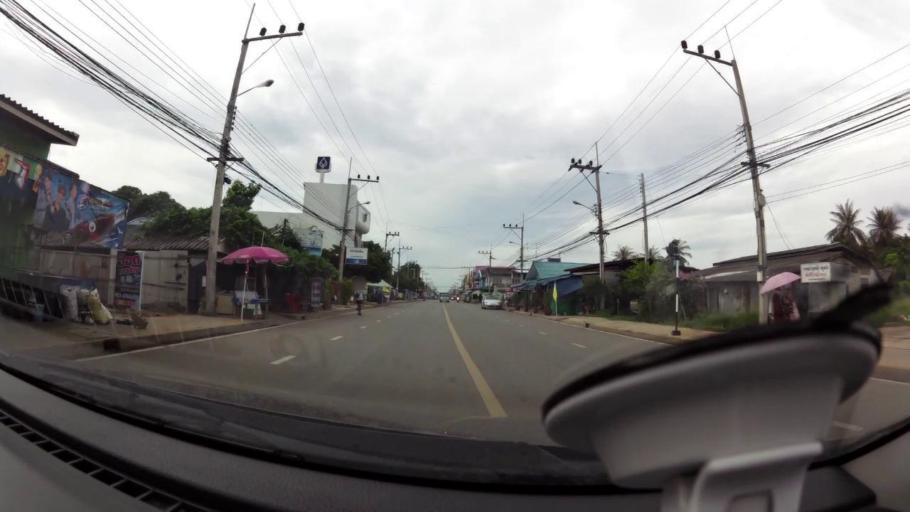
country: TH
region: Prachuap Khiri Khan
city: Pran Buri
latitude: 12.3983
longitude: 99.9901
